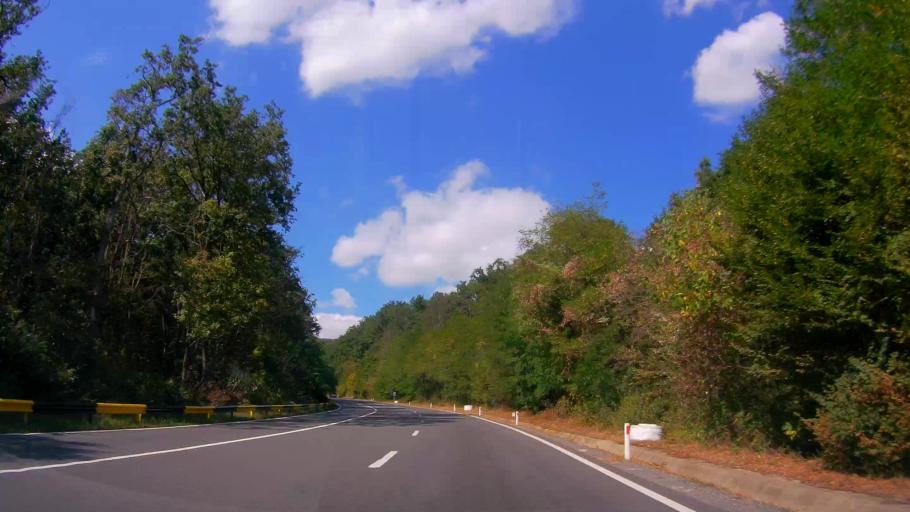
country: RO
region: Salaj
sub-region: Comuna Treznea
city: Treznea
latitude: 47.1384
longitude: 23.1187
